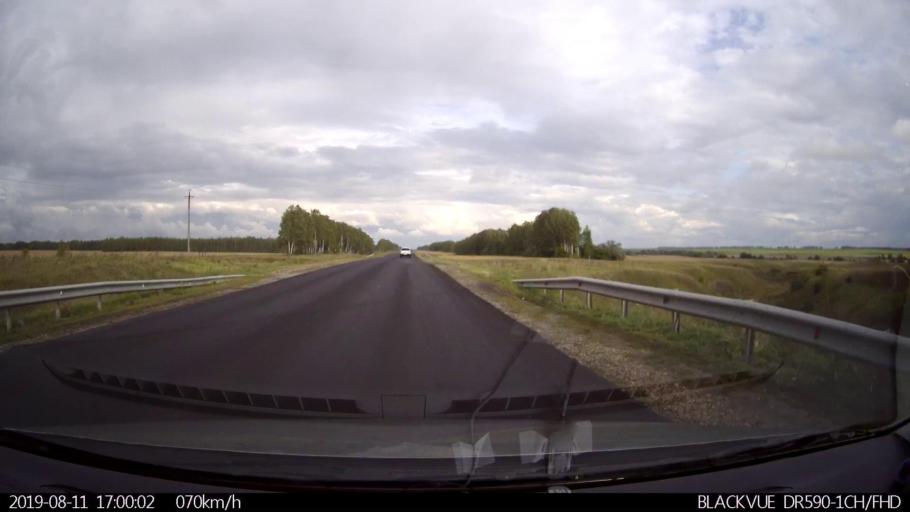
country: RU
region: Ulyanovsk
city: Mayna
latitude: 54.3112
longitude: 47.6722
